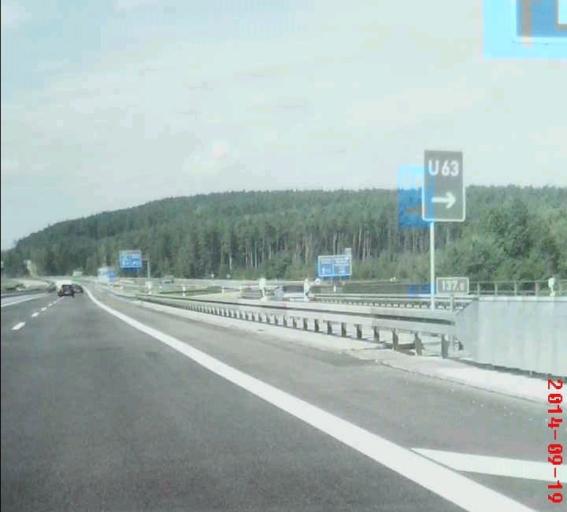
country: DE
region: Bavaria
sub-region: Upper Palatinate
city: Wernberg-Koblitz
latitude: 49.5143
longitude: 12.1686
